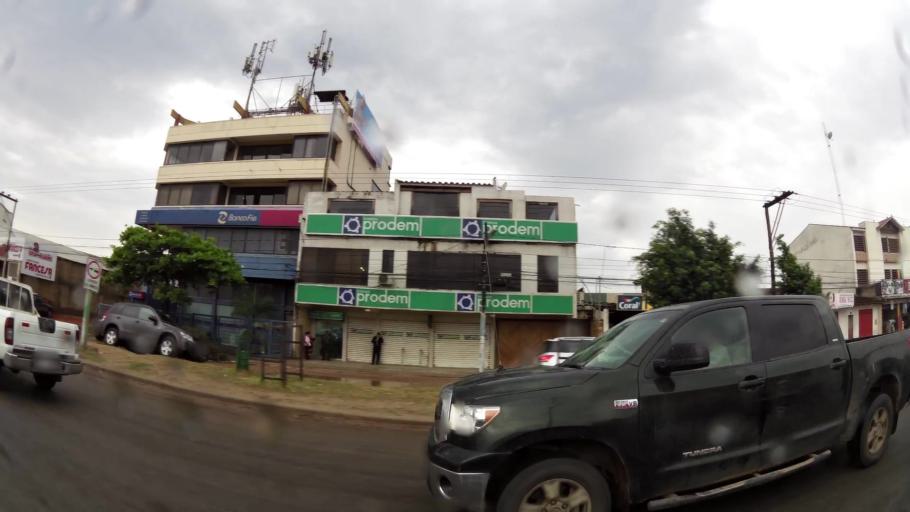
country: BO
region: Santa Cruz
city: Santa Cruz de la Sierra
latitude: -17.7687
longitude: -63.1185
